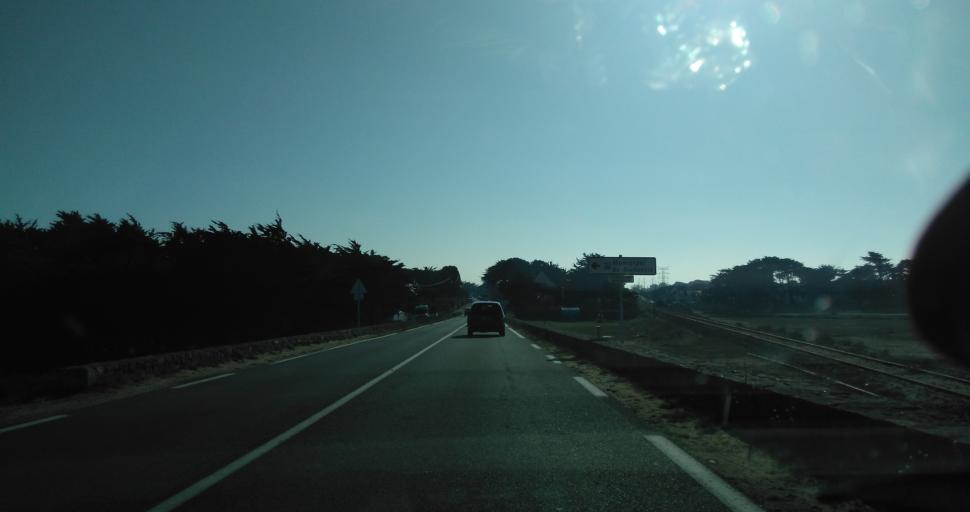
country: FR
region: Brittany
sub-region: Departement du Morbihan
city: Saint-Pierre-Quiberon
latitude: 47.5415
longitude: -3.1351
